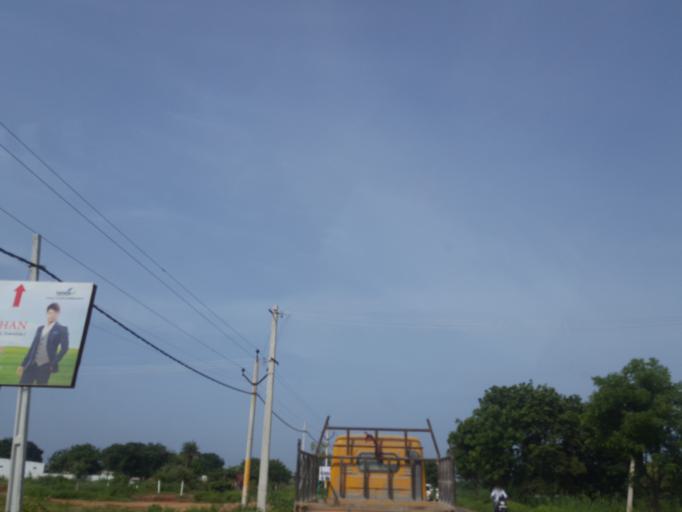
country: IN
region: Telangana
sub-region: Medak
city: Patancheru
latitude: 17.5092
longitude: 78.2159
